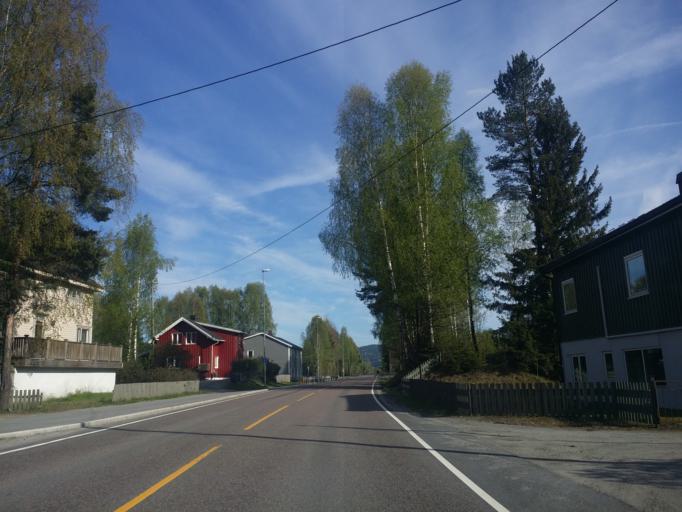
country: NO
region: Telemark
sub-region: Notodden
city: Notodden
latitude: 59.5911
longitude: 9.1522
